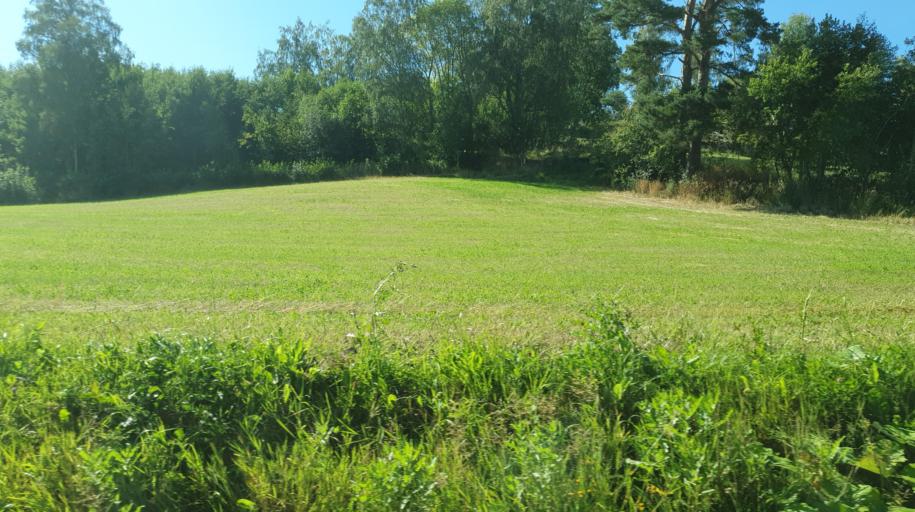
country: NO
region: Nord-Trondelag
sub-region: Verdal
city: Verdal
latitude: 63.7712
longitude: 11.4103
